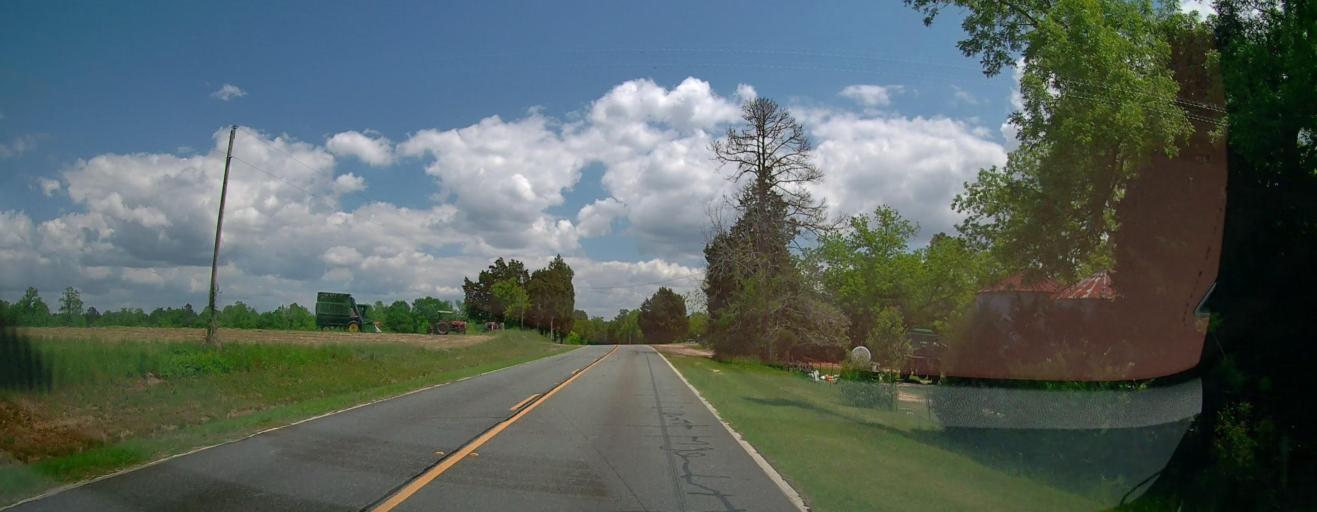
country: US
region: Georgia
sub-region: Treutlen County
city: Soperton
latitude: 32.5121
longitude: -82.6469
